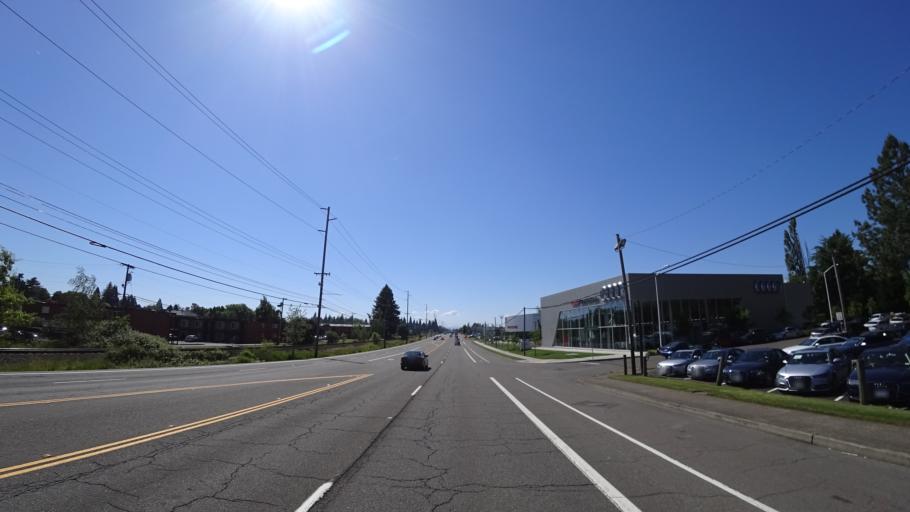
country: US
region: Oregon
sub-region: Washington County
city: Beaverton
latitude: 45.4887
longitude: -122.8173
